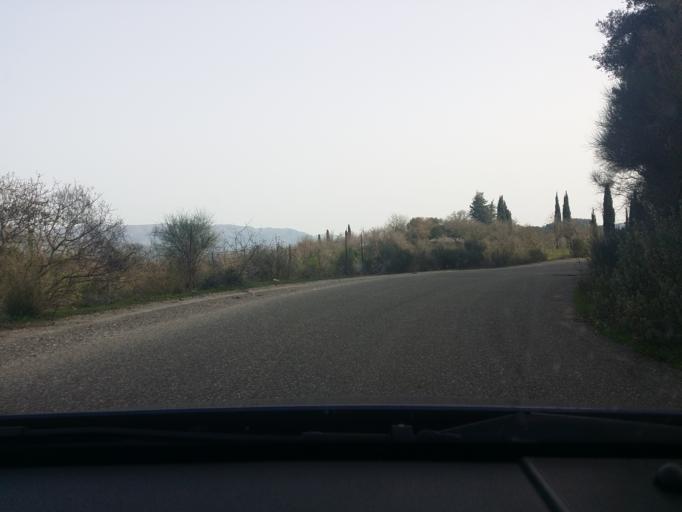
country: GR
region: West Greece
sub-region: Nomos Aitolias kai Akarnanias
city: Katouna
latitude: 38.8020
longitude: 21.0996
